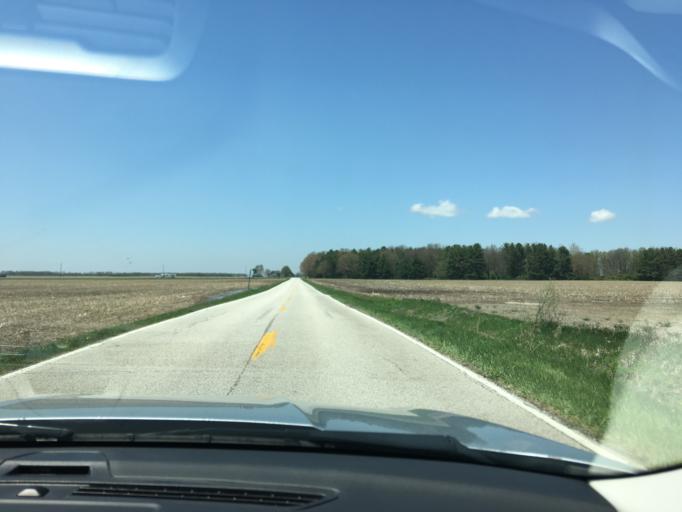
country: US
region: Indiana
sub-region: Tippecanoe County
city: Dayton
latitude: 40.3159
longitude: -86.7608
